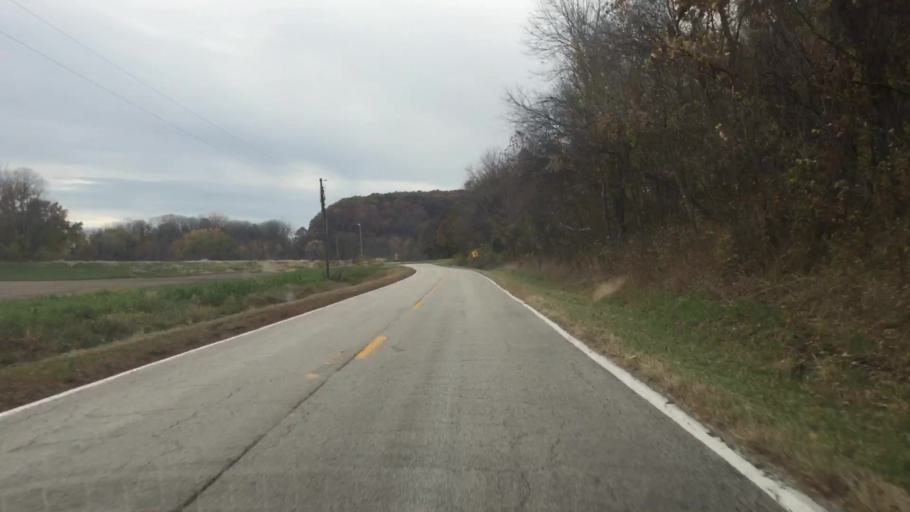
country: US
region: Missouri
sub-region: Gasconade County
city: Hermann
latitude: 38.7052
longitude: -91.6199
